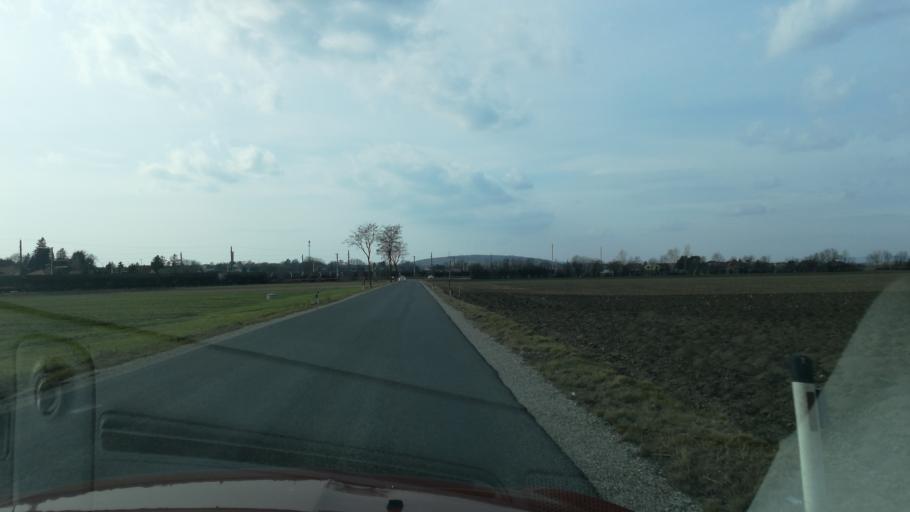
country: AT
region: Lower Austria
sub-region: Politischer Bezirk Tulln
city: Atzenbrugg
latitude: 48.3037
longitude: 15.9106
